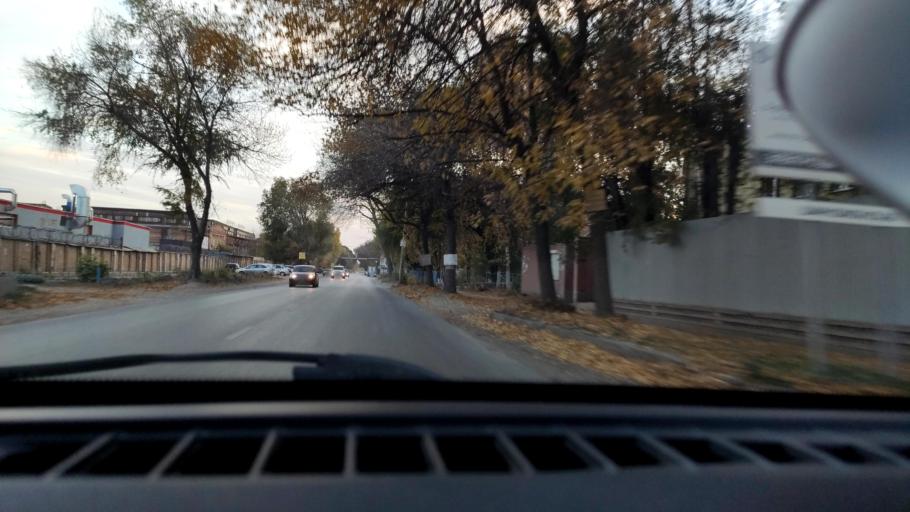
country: RU
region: Samara
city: Samara
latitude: 53.1895
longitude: 50.2451
